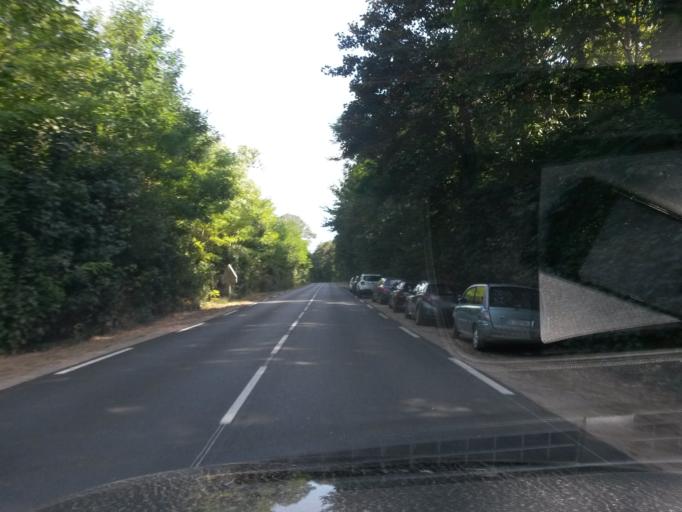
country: FR
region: Pays de la Loire
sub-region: Departement de la Vendee
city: Olonne-sur-Mer
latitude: 46.5673
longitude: -1.8193
